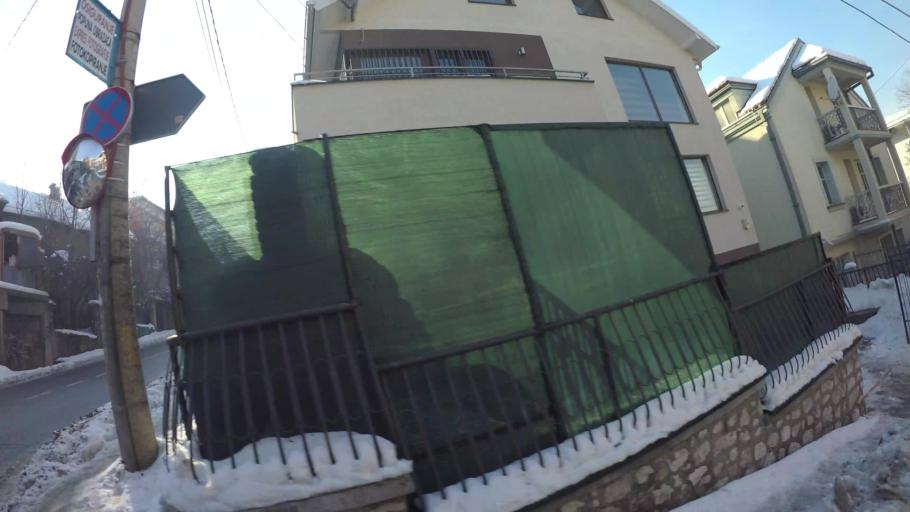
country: BA
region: Federation of Bosnia and Herzegovina
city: Kobilja Glava
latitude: 43.8511
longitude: 18.4045
